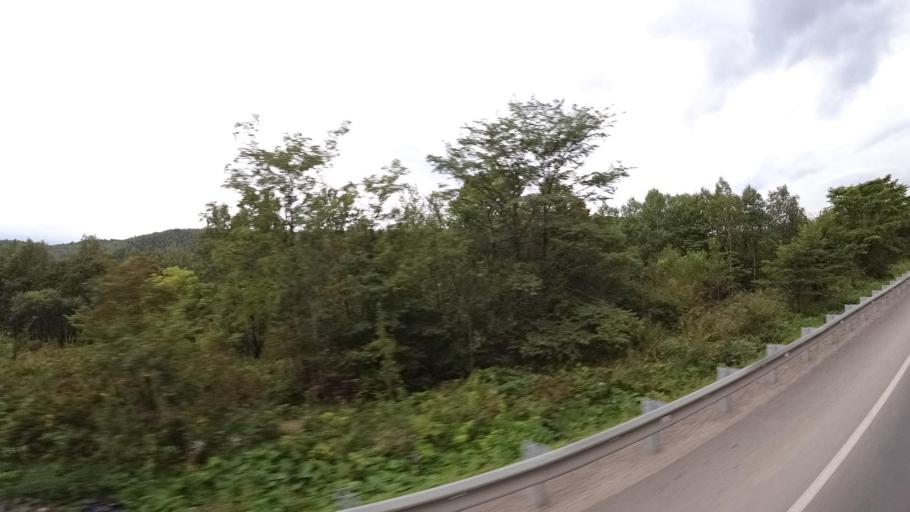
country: RU
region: Jewish Autonomous Oblast
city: Khingansk
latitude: 48.9884
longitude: 131.1306
